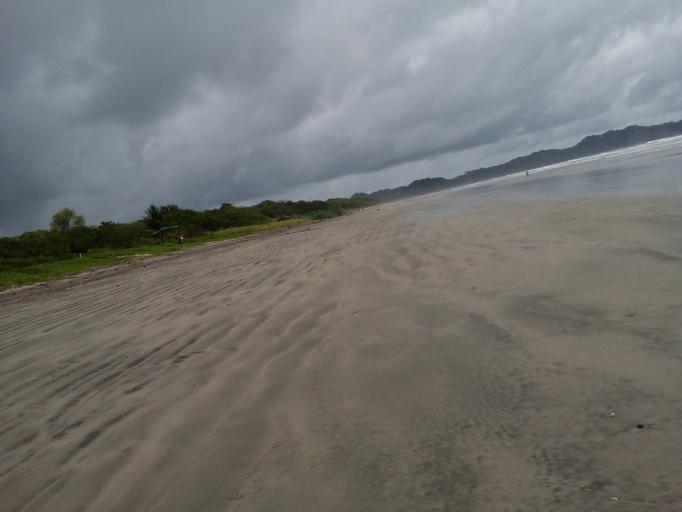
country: CR
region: Guanacaste
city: Samara
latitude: 9.9388
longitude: -85.6673
